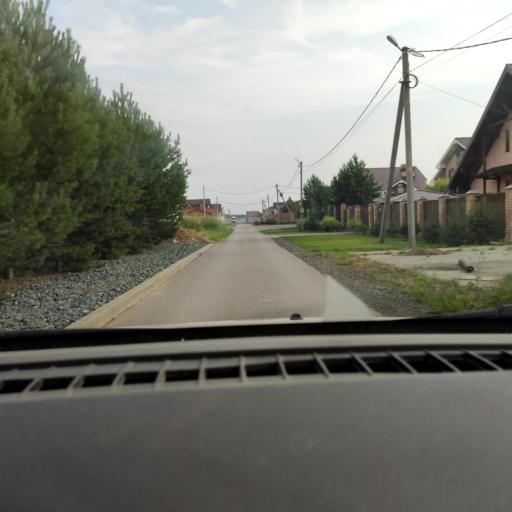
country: RU
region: Perm
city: Perm
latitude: 58.0392
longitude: 56.3760
